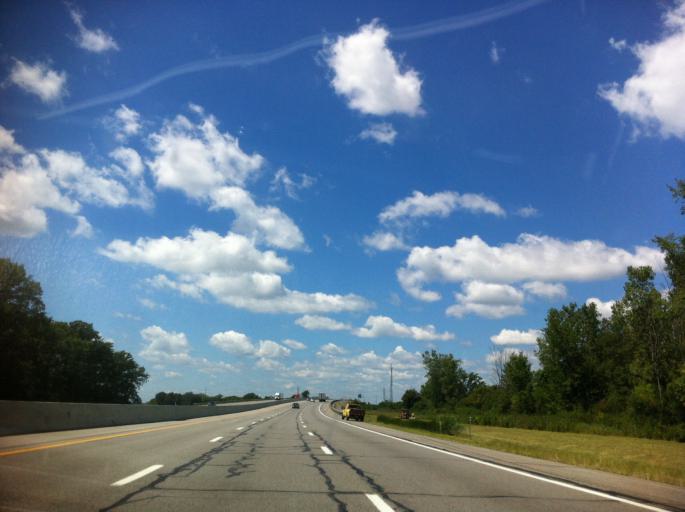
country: US
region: Ohio
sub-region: Wood County
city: Rossford
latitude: 41.5522
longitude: -83.5483
